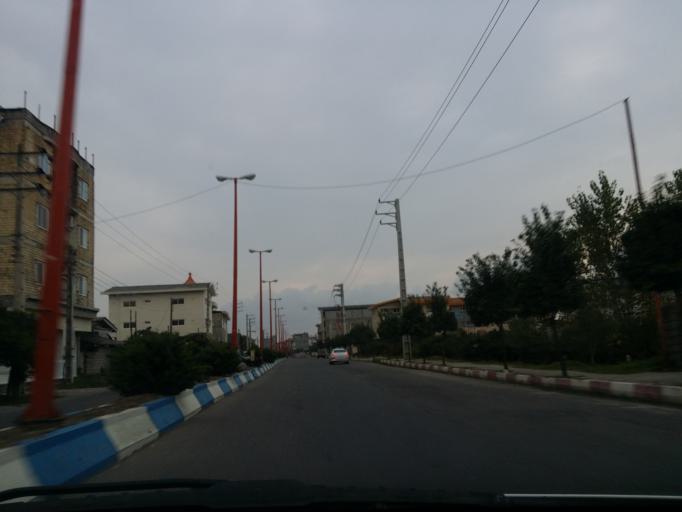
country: IR
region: Mazandaran
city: `Abbasabad
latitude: 36.7154
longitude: 51.1023
